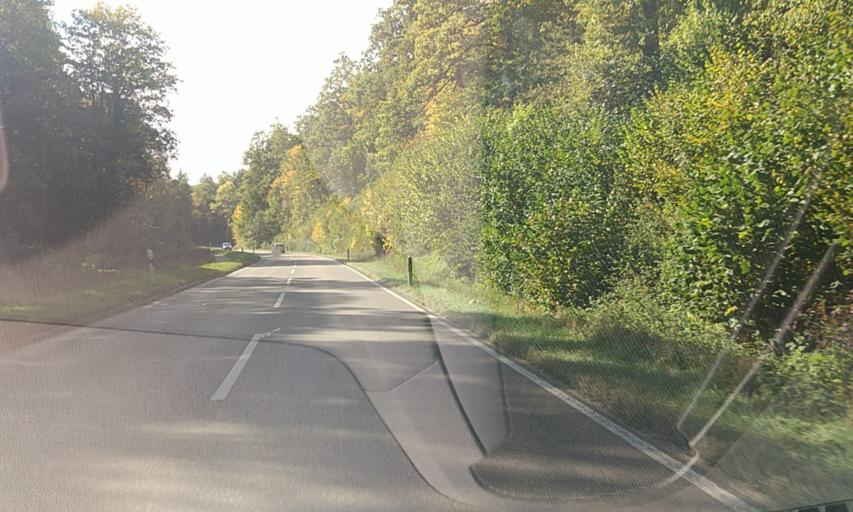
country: DE
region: Baden-Wuerttemberg
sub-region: Tuebingen Region
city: Dornstadt
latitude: 48.4295
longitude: 9.9283
